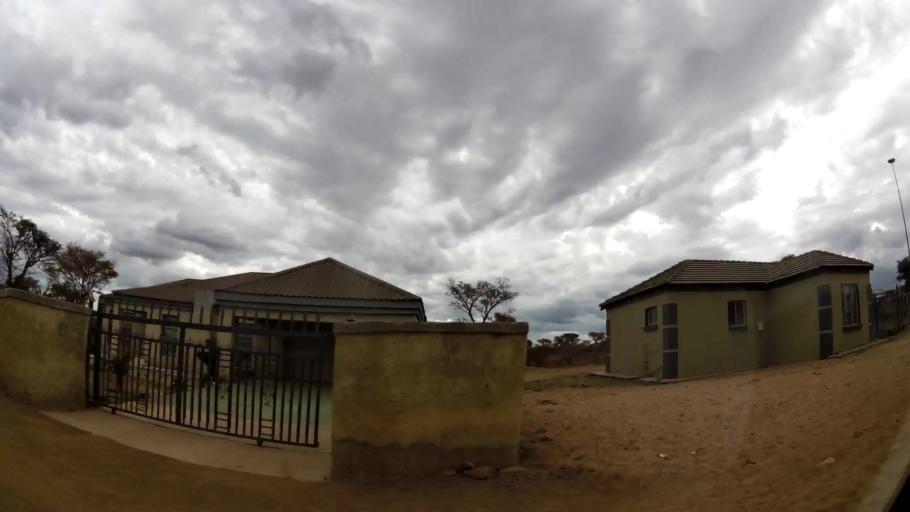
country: ZA
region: Limpopo
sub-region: Waterberg District Municipality
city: Modimolle
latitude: -24.6960
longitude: 28.4246
